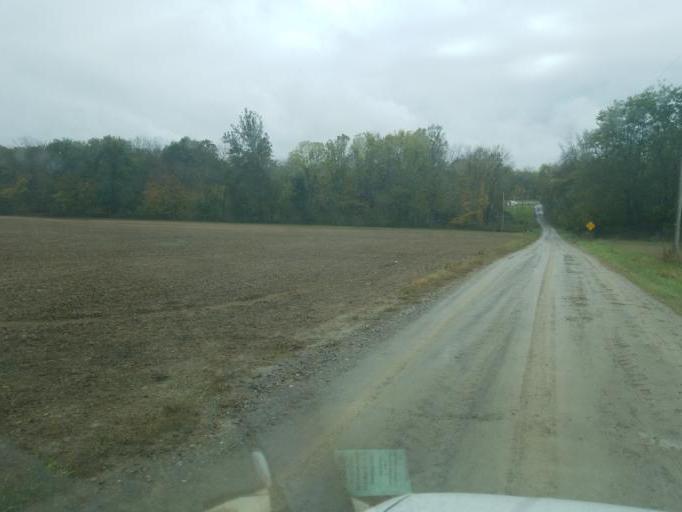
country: US
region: Ohio
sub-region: Holmes County
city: Millersburg
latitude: 40.5930
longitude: -81.9925
